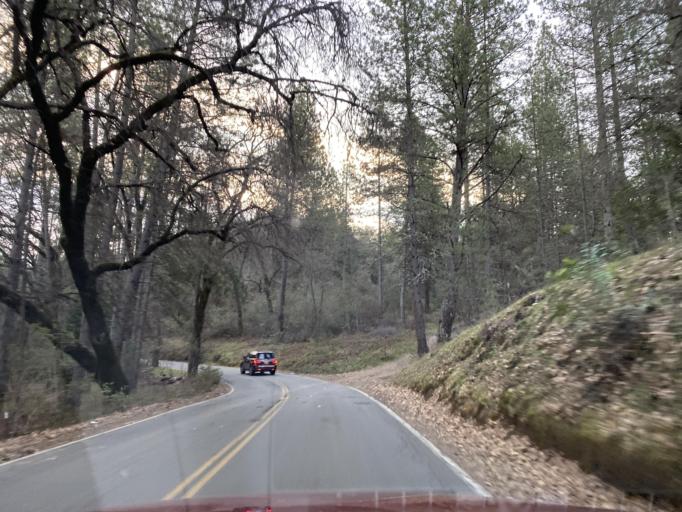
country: US
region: California
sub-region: Amador County
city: Pine Grove
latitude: 38.4982
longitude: -120.7041
